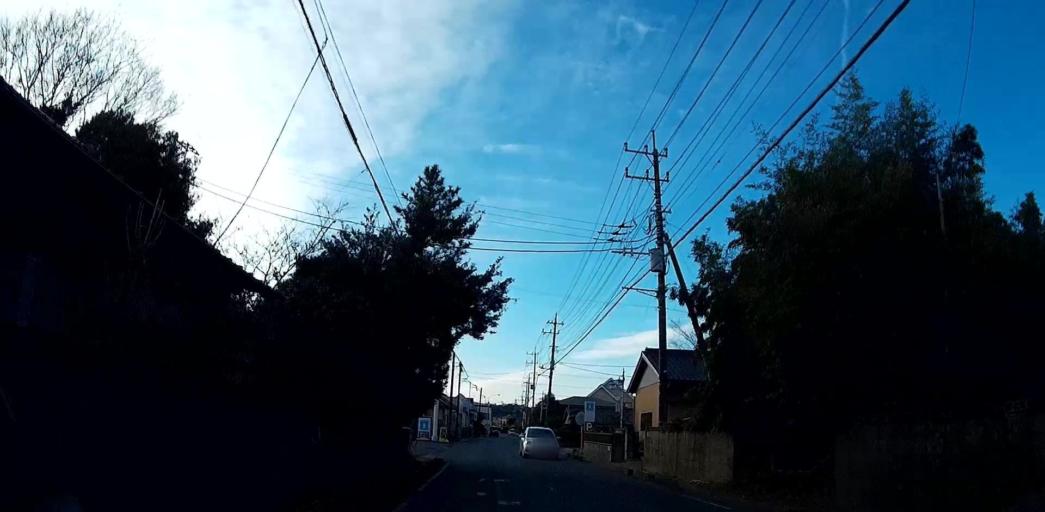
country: JP
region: Chiba
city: Omigawa
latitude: 35.8398
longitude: 140.6651
